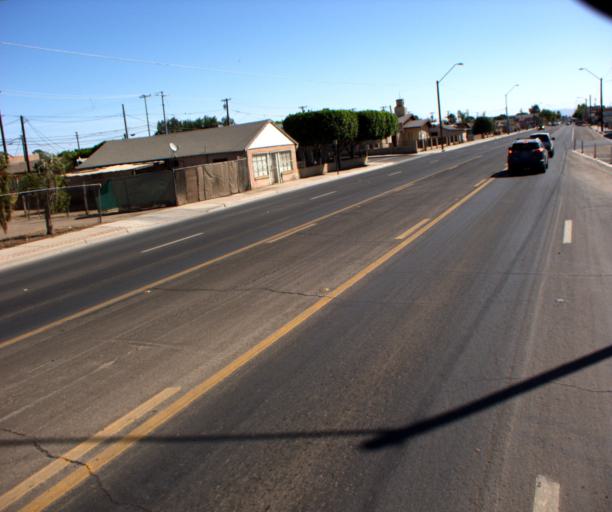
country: US
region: Arizona
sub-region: Yuma County
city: Somerton
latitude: 32.5966
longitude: -114.7169
